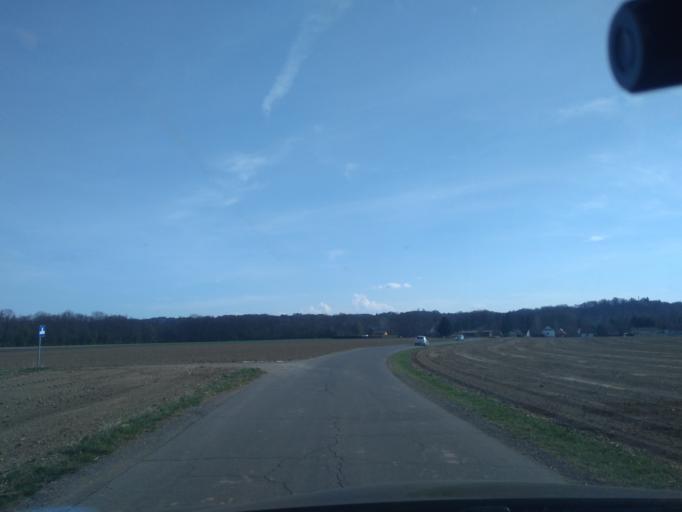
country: SI
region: Sentilj
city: Selnica ob Muri
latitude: 46.7098
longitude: 15.7302
